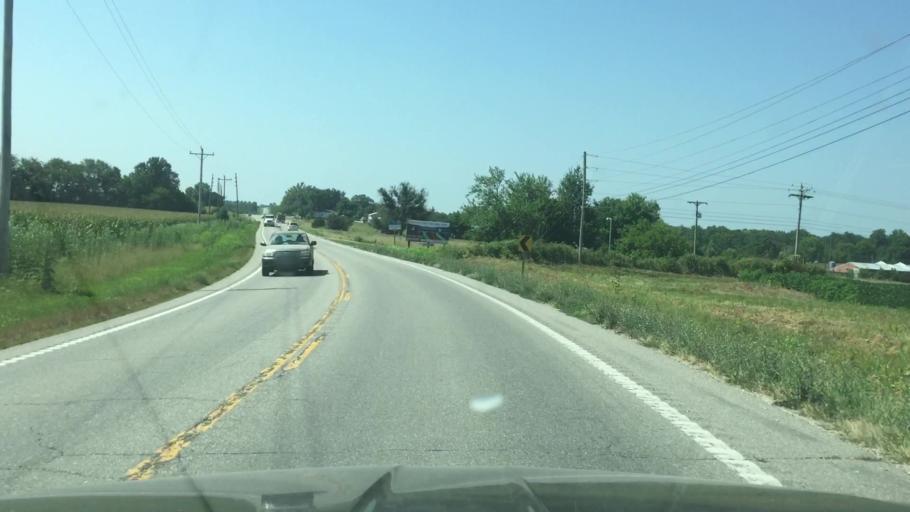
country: US
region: Missouri
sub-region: Moniteau County
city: Tipton
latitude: 38.6402
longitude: -92.7890
